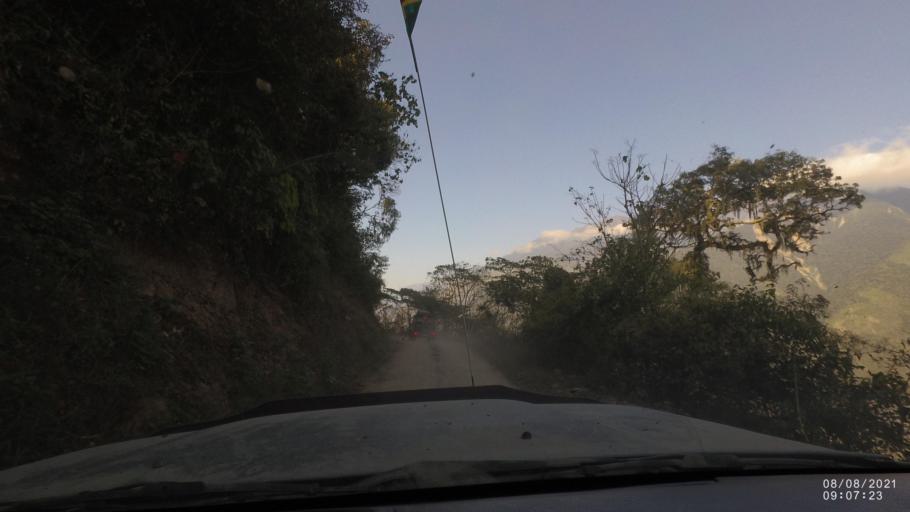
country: BO
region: La Paz
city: Quime
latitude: -16.5617
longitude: -66.7324
